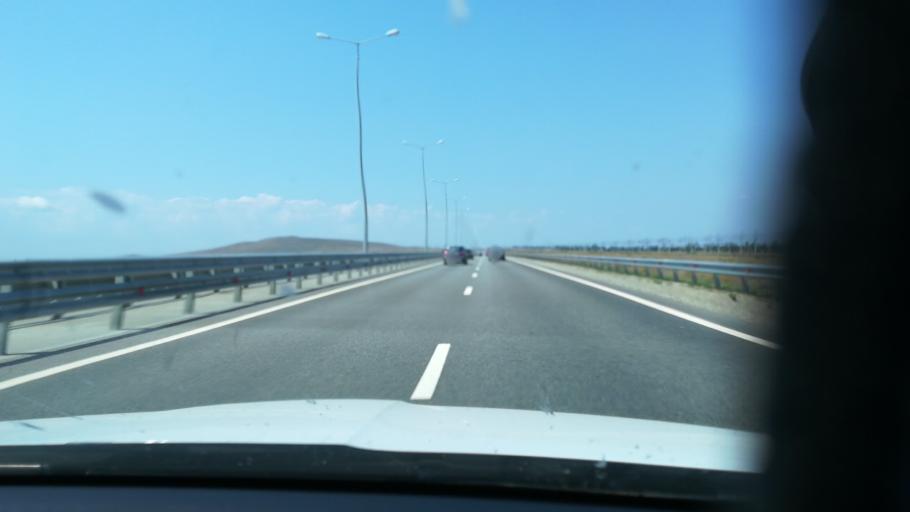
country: RU
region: Krasnodarskiy
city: Vyshestebliyevskaya
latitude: 45.2296
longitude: 36.9247
